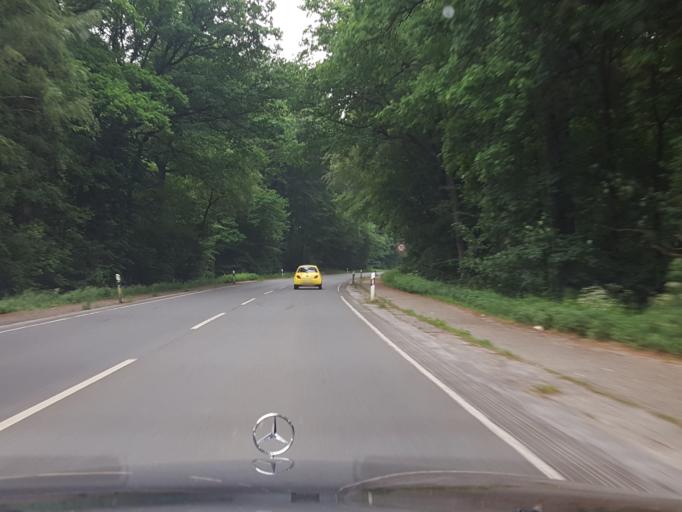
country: DE
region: North Rhine-Westphalia
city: Oer-Erkenschwick
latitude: 51.6815
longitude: 7.2958
